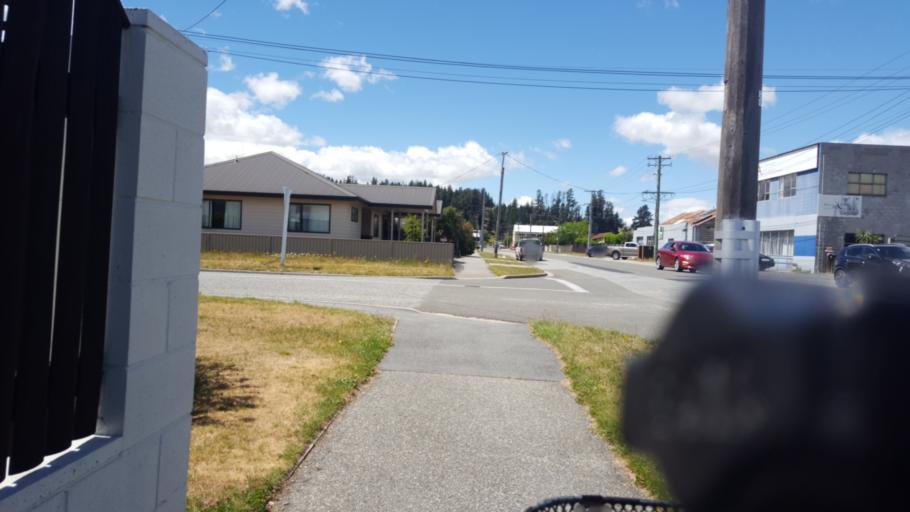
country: NZ
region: Otago
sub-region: Queenstown-Lakes District
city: Wanaka
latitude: -45.2472
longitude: 169.3925
